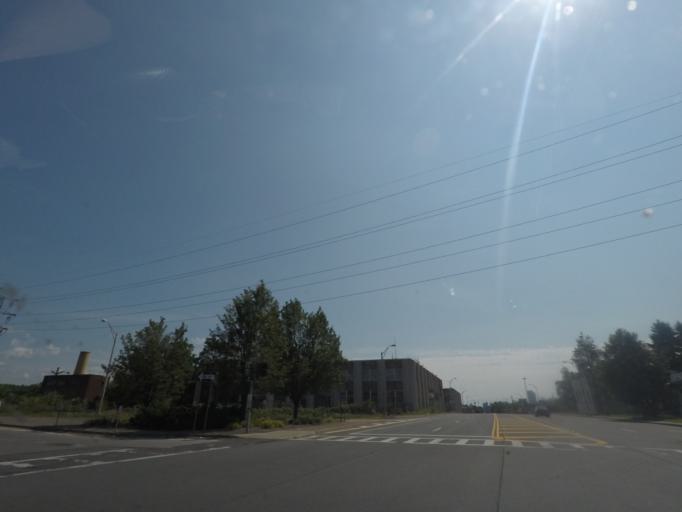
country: US
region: New York
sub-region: Albany County
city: Menands
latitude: 42.6853
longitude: -73.7298
